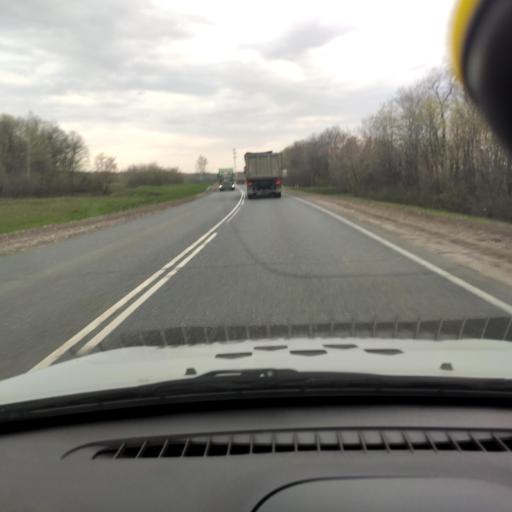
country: RU
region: Samara
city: Zhigulevsk
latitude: 53.2904
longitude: 49.3287
